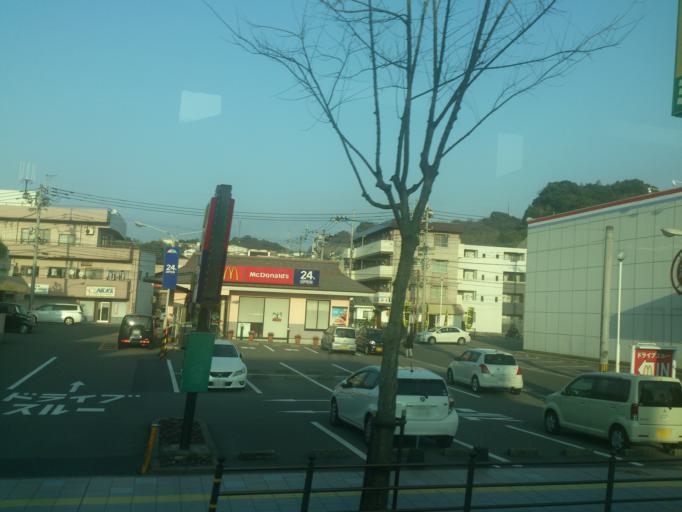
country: JP
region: Kagoshima
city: Kagoshima-shi
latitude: 31.6013
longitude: 130.5392
